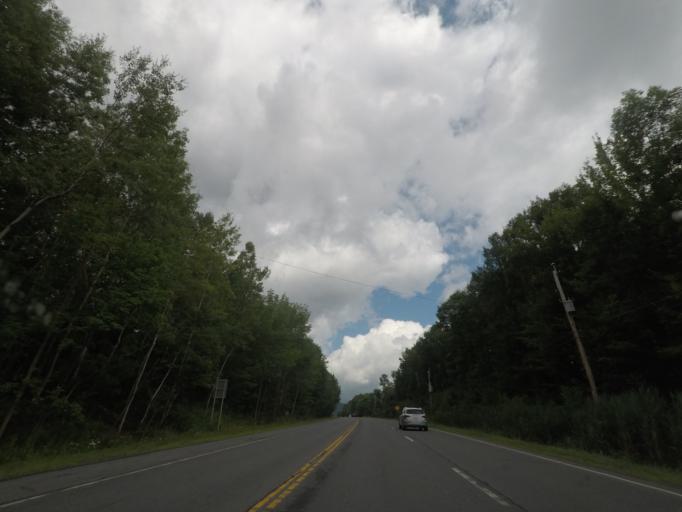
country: US
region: Massachusetts
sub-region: Berkshire County
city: Lanesborough
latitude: 42.5999
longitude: -73.3702
